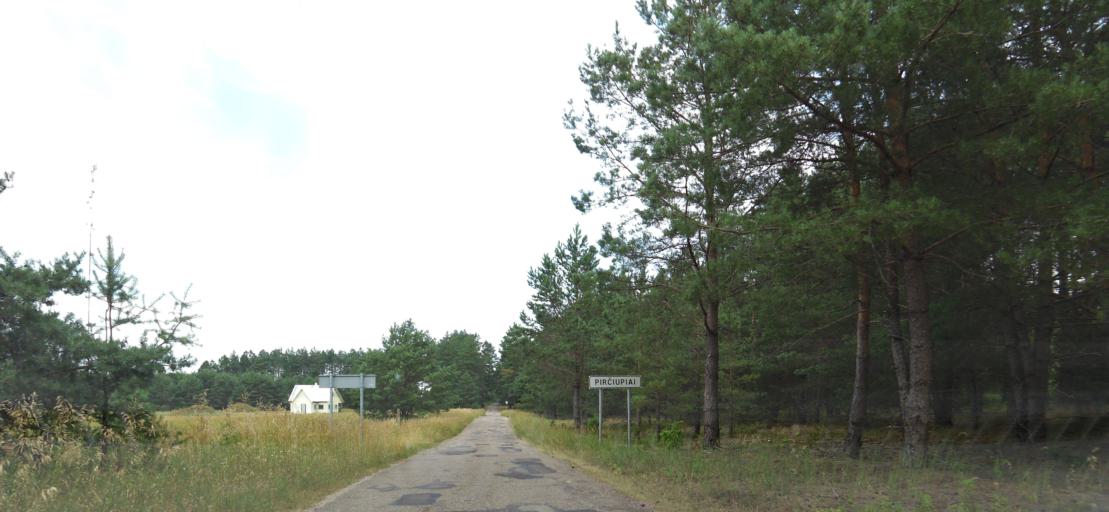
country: LT
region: Vilnius County
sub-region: Trakai
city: Rudiskes
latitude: 54.3956
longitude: 24.9601
